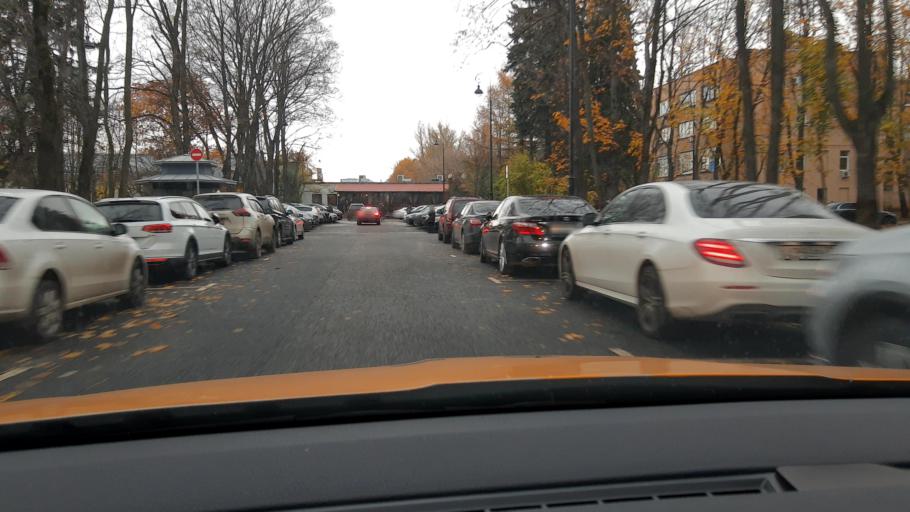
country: RU
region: Moskovskaya
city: Levoberezhnyy
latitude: 55.8539
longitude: 37.4665
